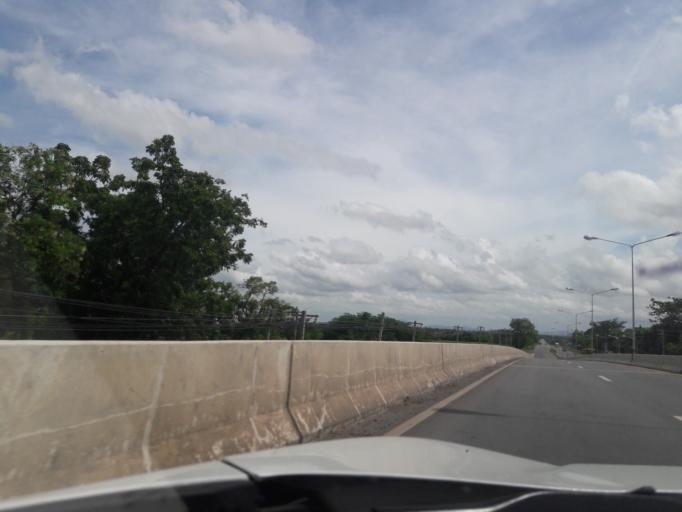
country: TH
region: Lop Buri
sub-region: Amphoe Tha Luang
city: Tha Luang
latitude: 15.0790
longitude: 101.0169
